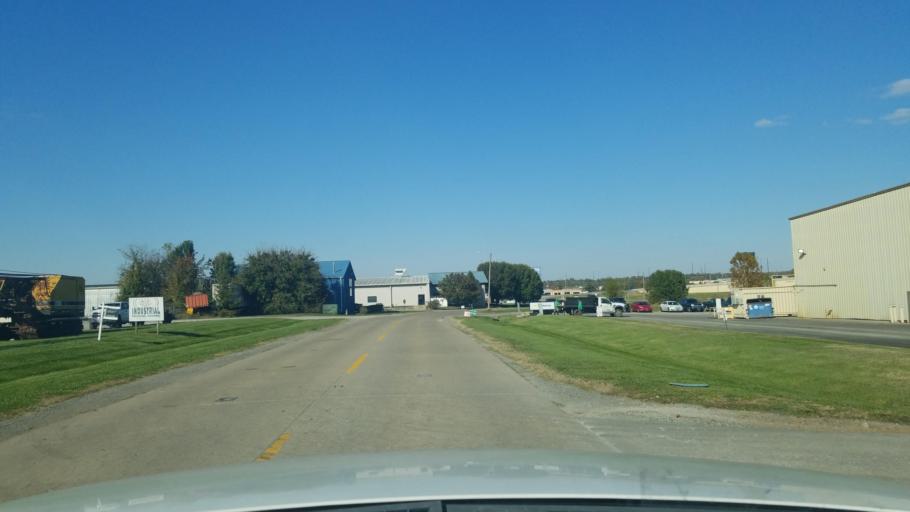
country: US
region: Illinois
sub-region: Williamson County
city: Marion
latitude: 37.7409
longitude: -88.9847
